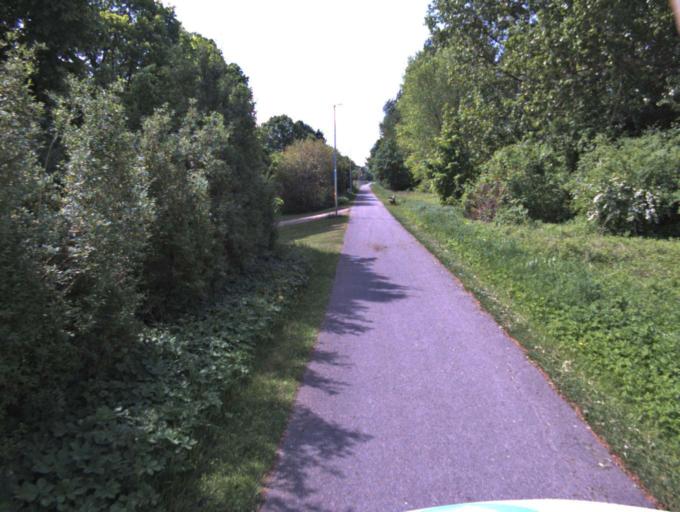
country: SE
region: Skane
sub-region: Kristianstads Kommun
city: Kristianstad
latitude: 56.0502
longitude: 14.1679
